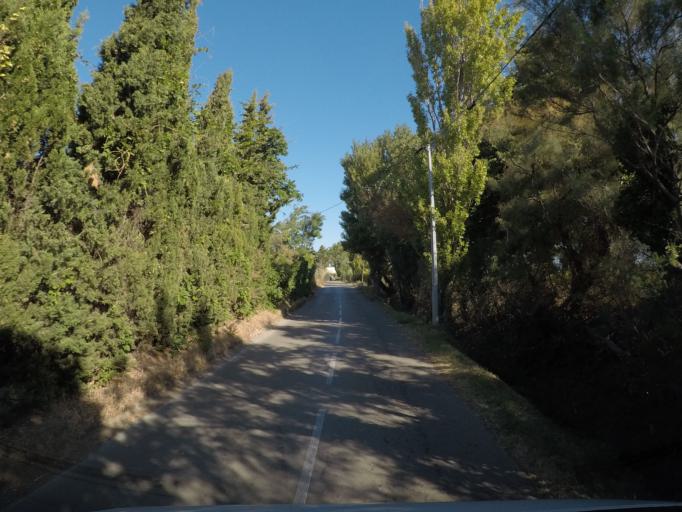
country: FR
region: Languedoc-Roussillon
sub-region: Departement de l'Aude
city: Narbonne
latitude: 43.1668
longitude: 3.0100
